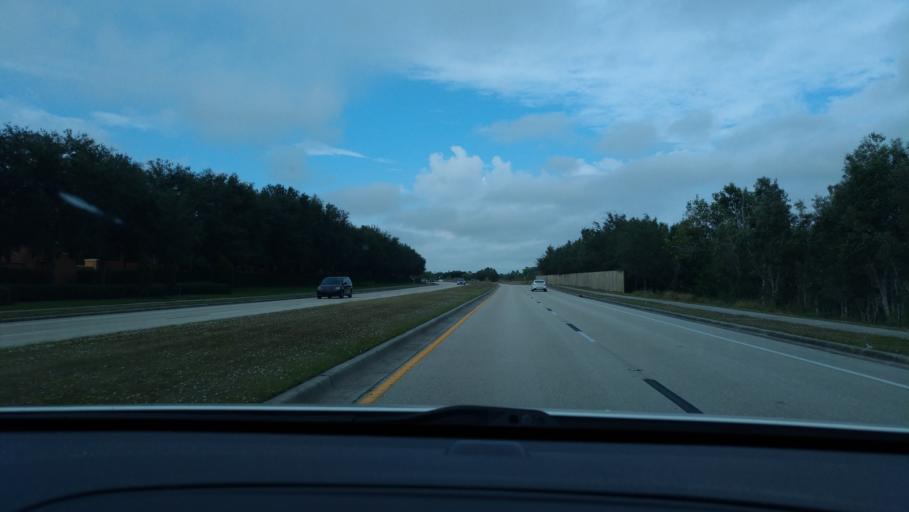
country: US
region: Florida
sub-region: Lee County
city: Estero
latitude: 26.4132
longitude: -81.8047
